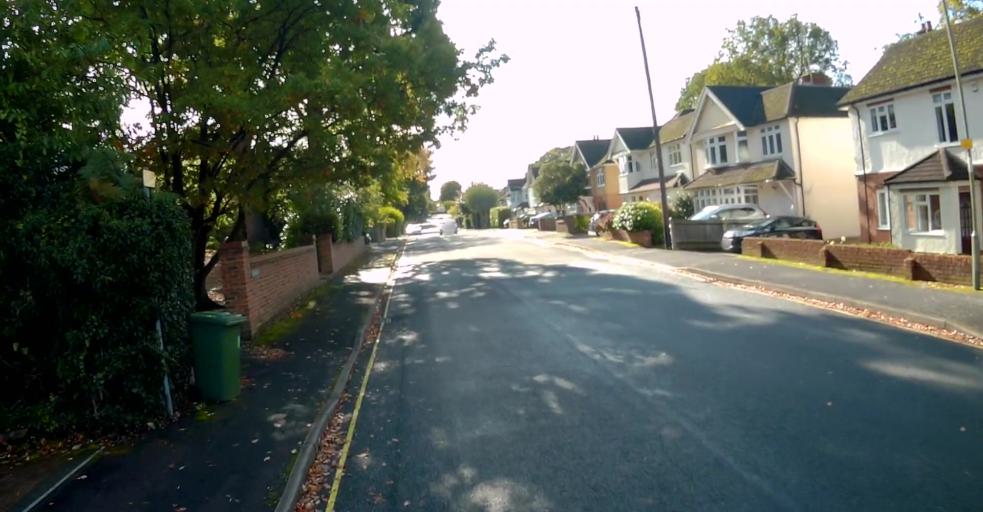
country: GB
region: England
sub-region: Hampshire
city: Farnborough
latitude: 51.2902
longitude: -0.7512
